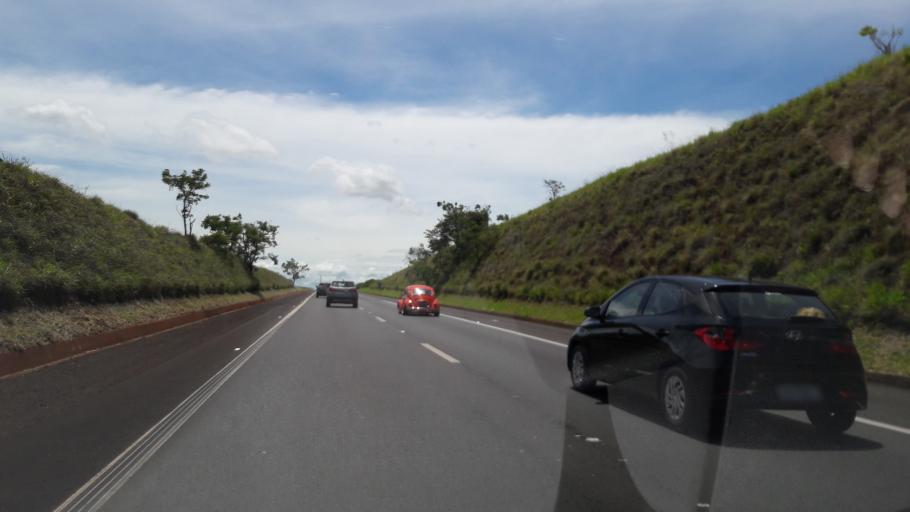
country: BR
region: Sao Paulo
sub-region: Avare
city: Avare
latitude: -22.9557
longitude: -48.8395
